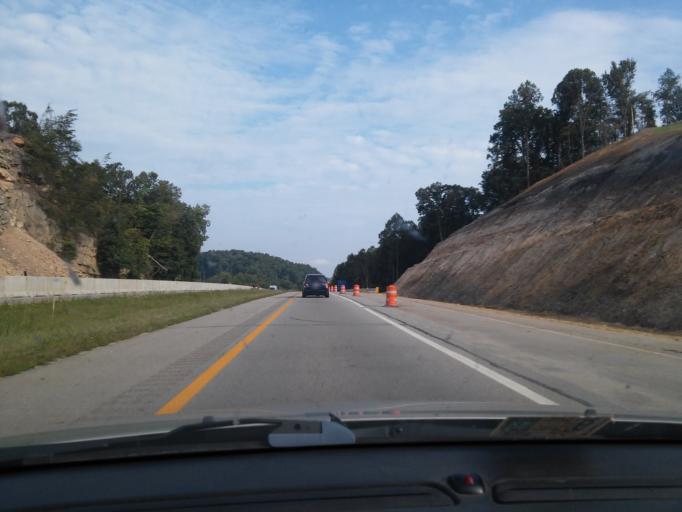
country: US
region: Ohio
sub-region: Jackson County
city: Jackson
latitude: 39.1089
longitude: -82.6772
